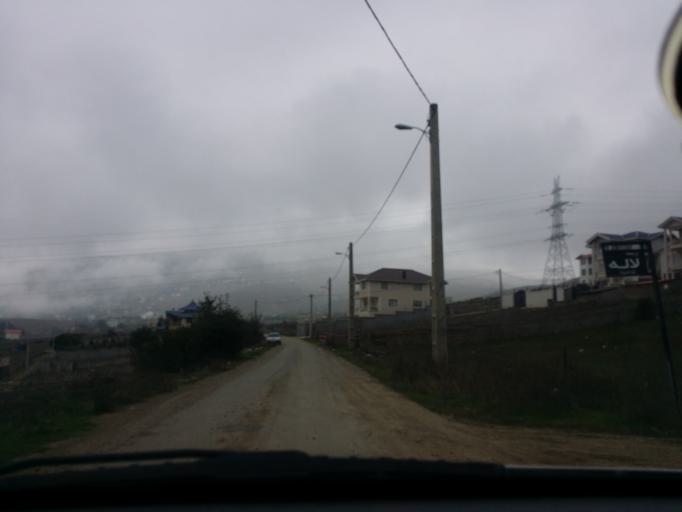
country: IR
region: Mazandaran
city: Chalus
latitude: 36.5117
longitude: 51.2289
